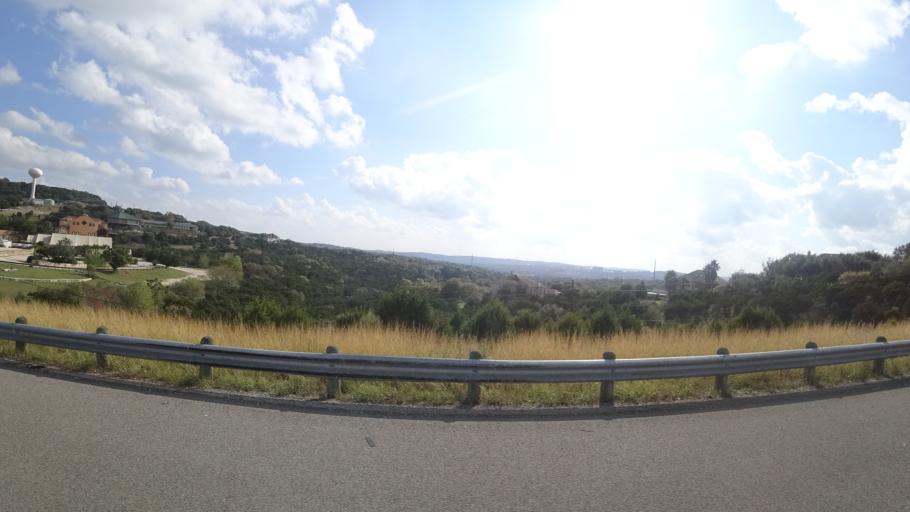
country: US
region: Texas
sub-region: Travis County
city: Lost Creek
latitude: 30.3101
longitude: -97.8469
